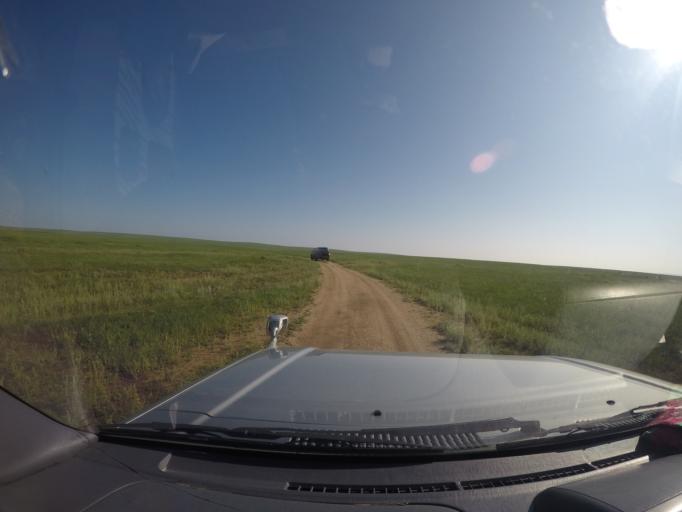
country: MN
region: Suhbaatar
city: Hanhohiy
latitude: 47.5733
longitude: 112.2267
